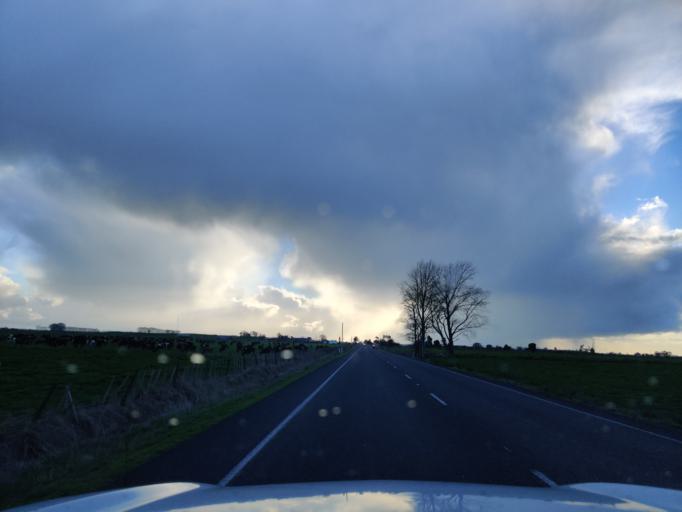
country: NZ
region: Waikato
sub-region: Hamilton City
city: Hamilton
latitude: -37.6942
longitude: 175.4345
